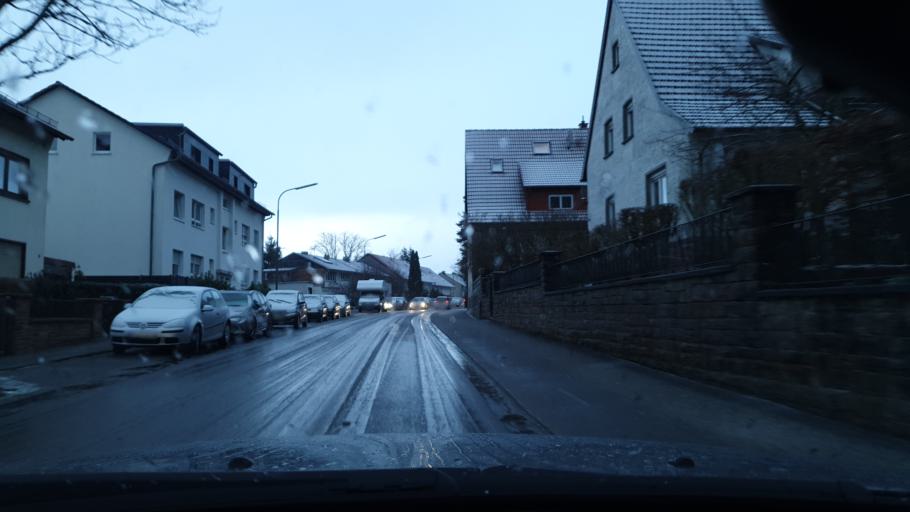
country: DE
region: Rheinland-Pfalz
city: Stelzenberg
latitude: 49.4202
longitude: 7.7045
